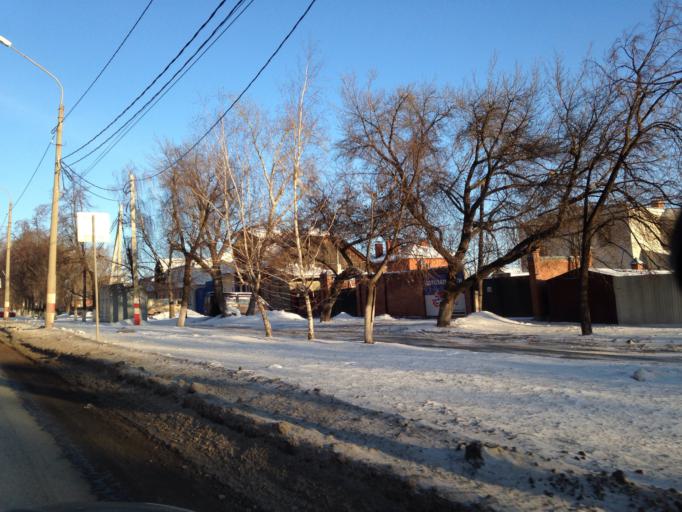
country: RU
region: Ulyanovsk
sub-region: Ulyanovskiy Rayon
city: Ulyanovsk
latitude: 54.3016
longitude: 48.3841
